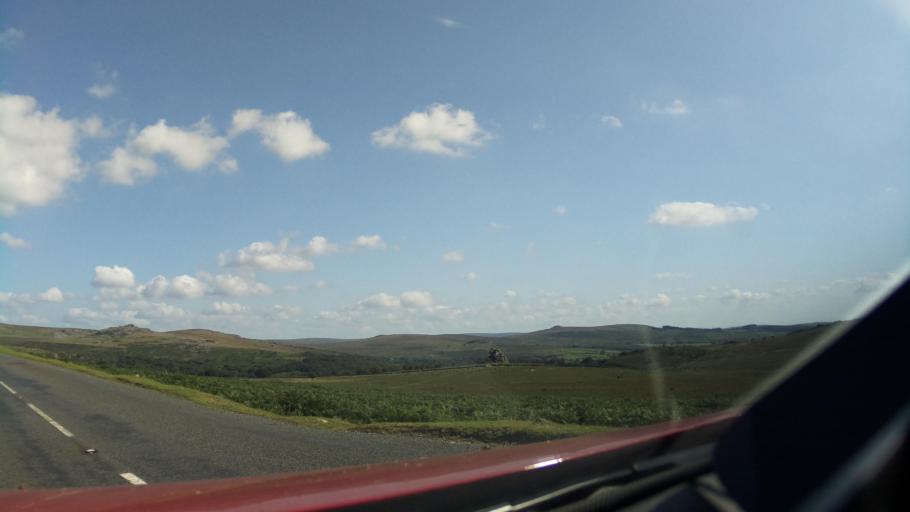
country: GB
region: England
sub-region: Devon
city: Horrabridge
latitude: 50.5562
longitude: -4.0665
